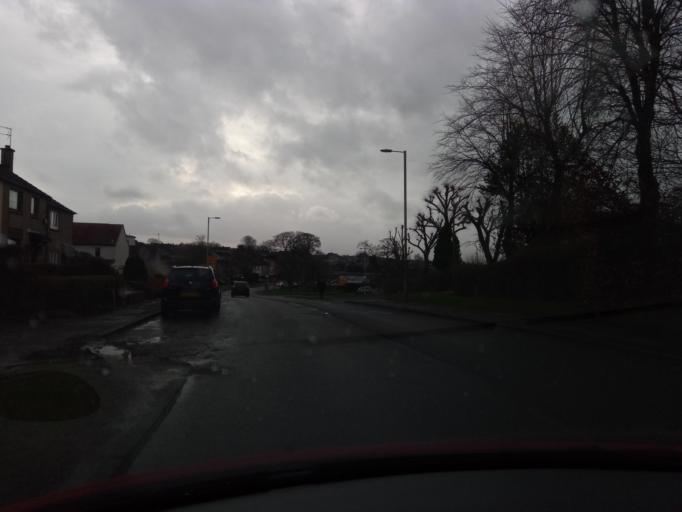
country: GB
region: Scotland
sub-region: East Dunbartonshire
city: Kirkintilloch
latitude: 55.9273
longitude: -4.1660
